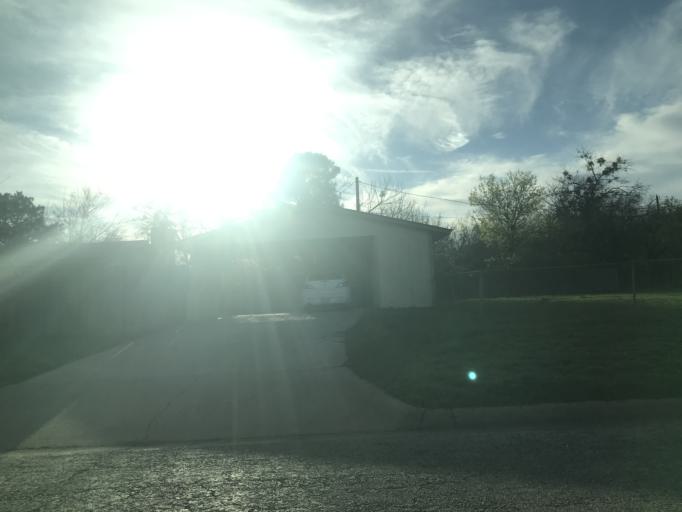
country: US
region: Texas
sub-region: Taylor County
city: Abilene
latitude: 32.4343
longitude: -99.7664
